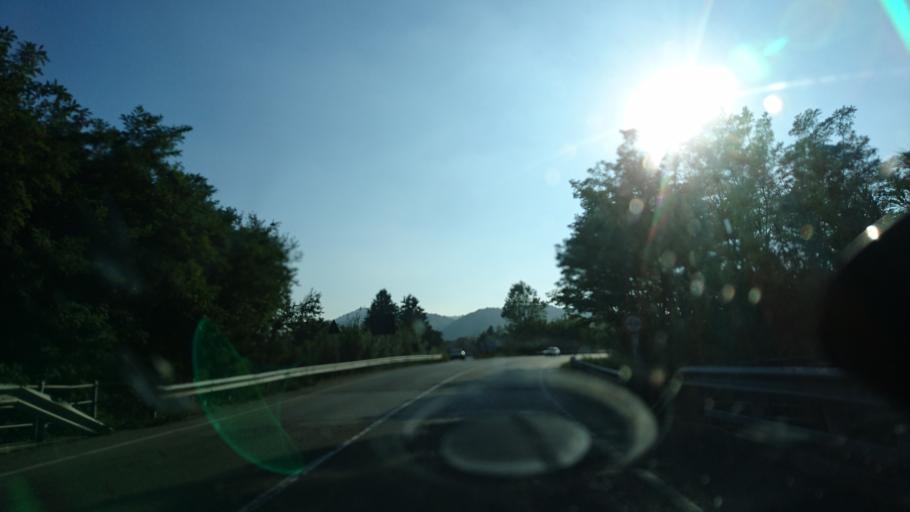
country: IT
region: Piedmont
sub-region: Provincia di Alessandria
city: Terzo
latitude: 44.6664
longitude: 8.4217
